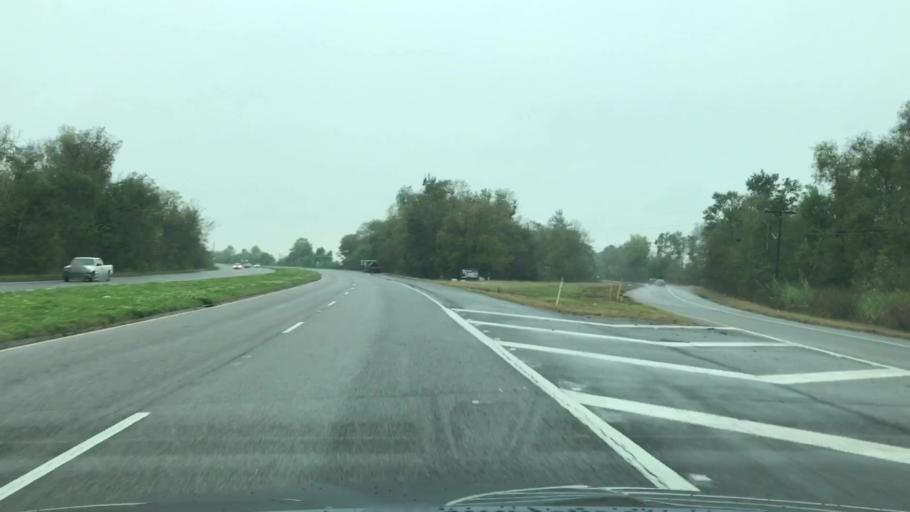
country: US
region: Louisiana
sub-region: Lafourche Parish
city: Raceland
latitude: 29.7608
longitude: -90.5518
